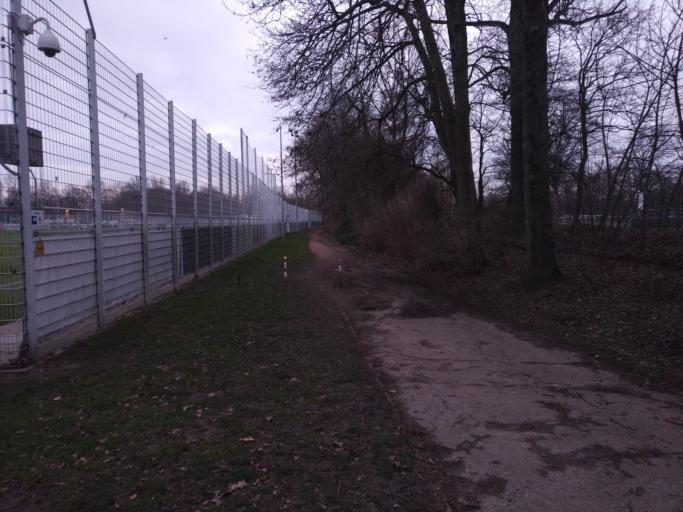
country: DE
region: North Rhine-Westphalia
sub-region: Regierungsbezirk Koln
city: Leverkusen
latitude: 51.0382
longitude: 6.9972
